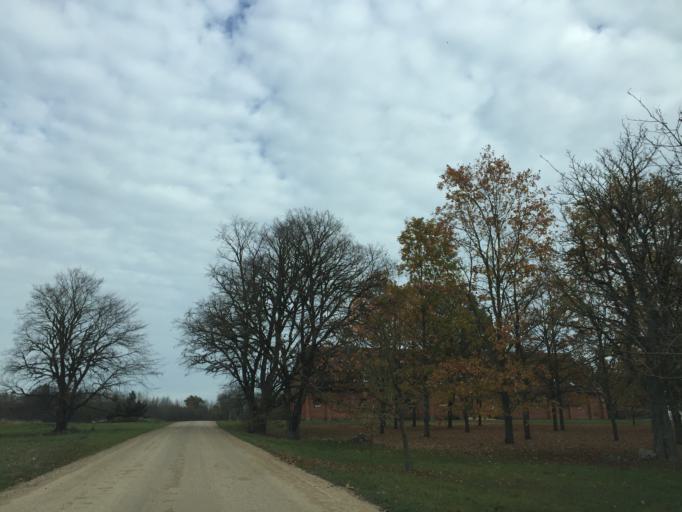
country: LV
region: Tukuma Rajons
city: Tukums
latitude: 56.9815
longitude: 23.0517
